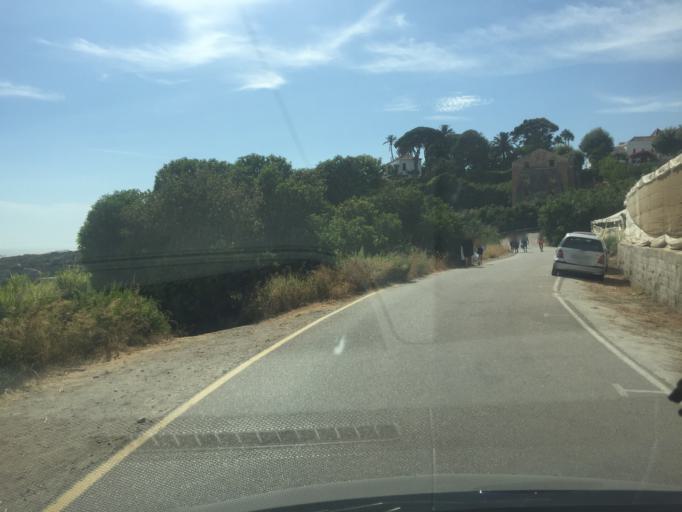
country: ES
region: Andalusia
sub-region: Provincia de Malaga
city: Nerja
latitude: 36.7560
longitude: -3.8407
